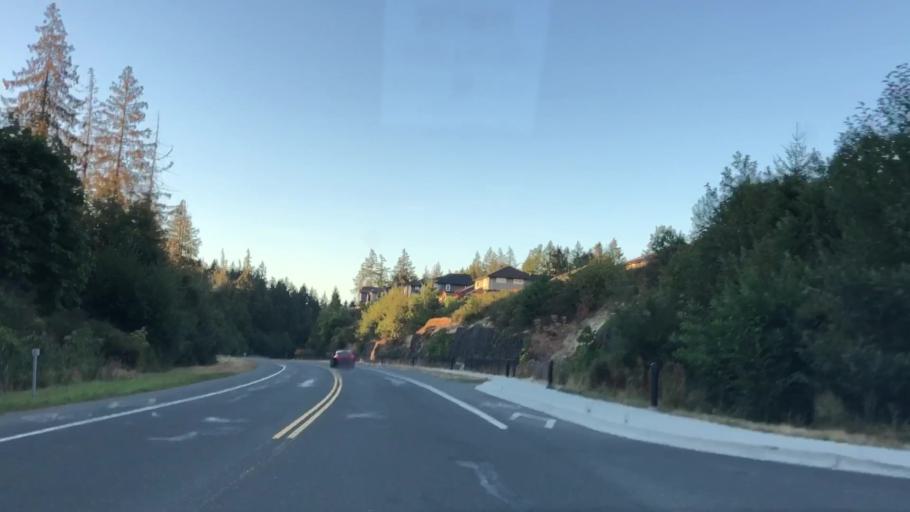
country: CA
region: British Columbia
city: Colwood
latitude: 48.4182
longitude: -123.5056
